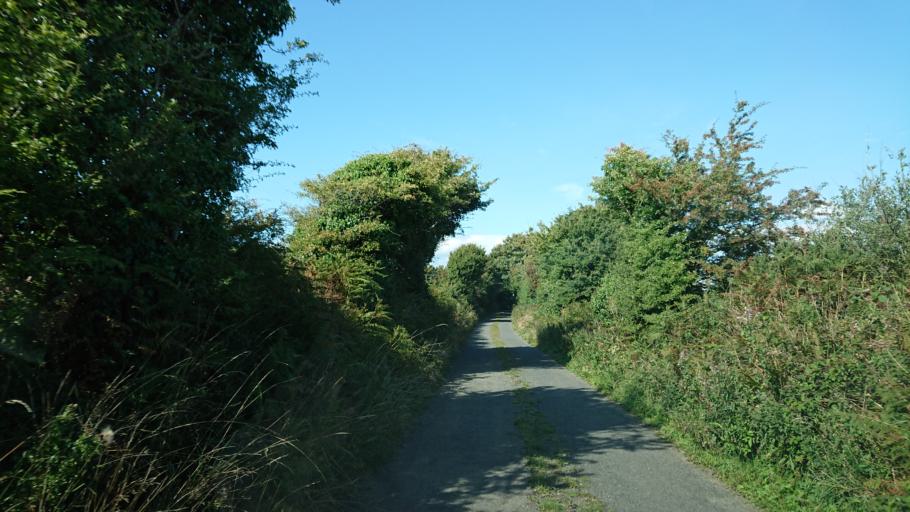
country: IE
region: Munster
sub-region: Waterford
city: Waterford
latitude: 52.2046
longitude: -7.0580
